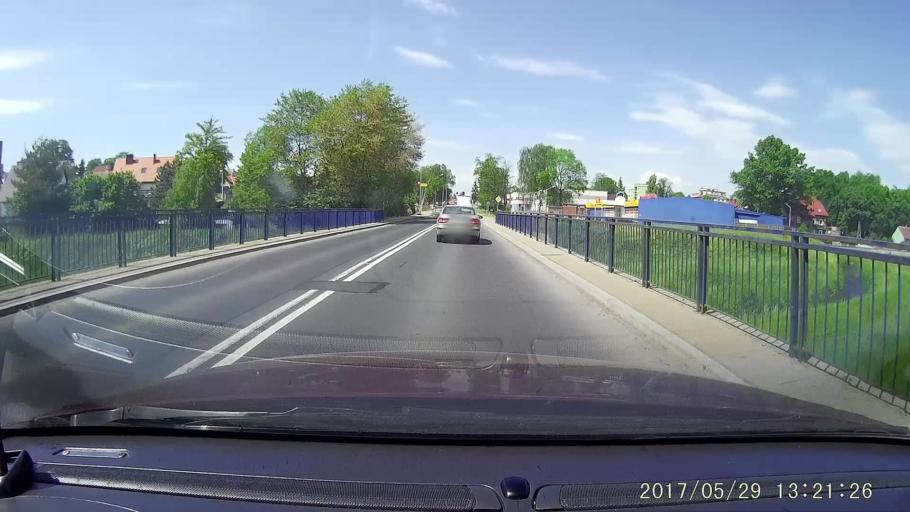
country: PL
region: Lower Silesian Voivodeship
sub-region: Powiat lwowecki
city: Gryfow Slaski
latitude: 51.0301
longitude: 15.4218
